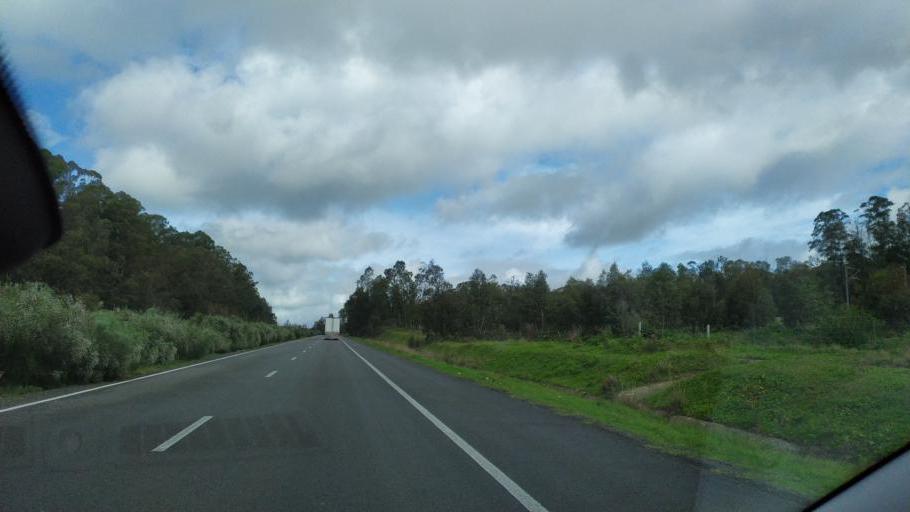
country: MA
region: Gharb-Chrarda-Beni Hssen
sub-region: Kenitra Province
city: Lalla Mimouna
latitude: 34.9272
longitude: -6.2026
